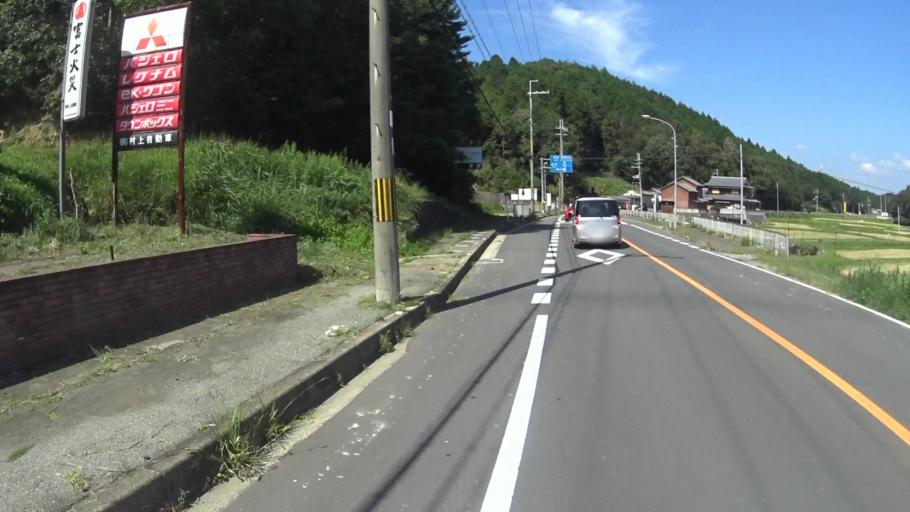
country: JP
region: Kyoto
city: Kameoka
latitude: 34.9715
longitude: 135.5173
